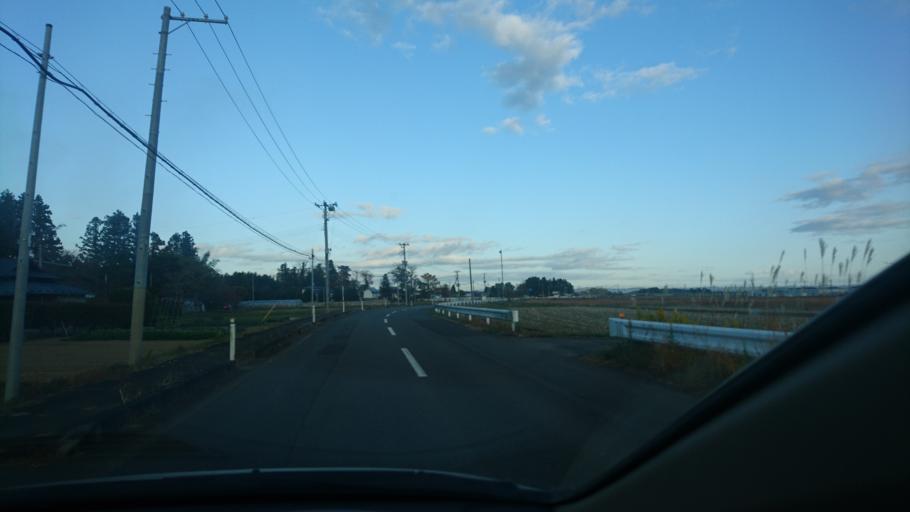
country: JP
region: Iwate
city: Ichinoseki
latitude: 38.7742
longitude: 141.0696
